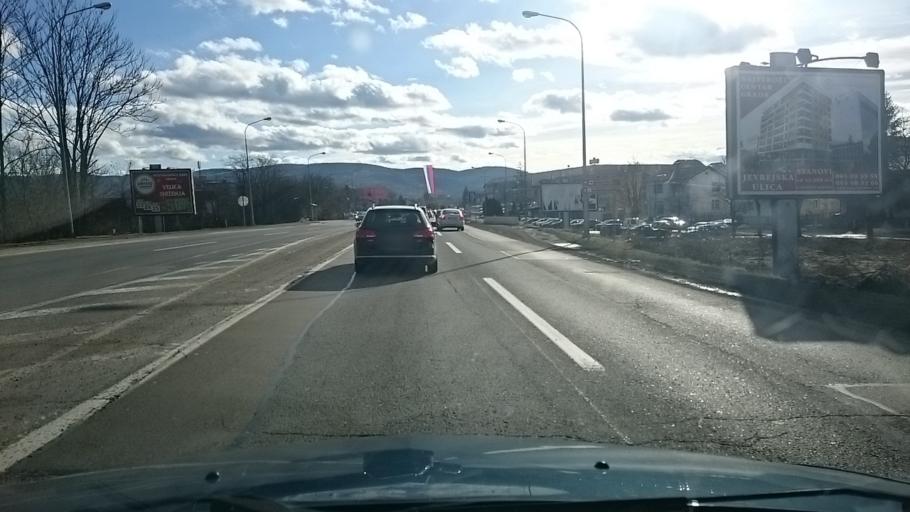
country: BA
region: Republika Srpska
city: Banja Luka
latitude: 44.7928
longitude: 17.1995
